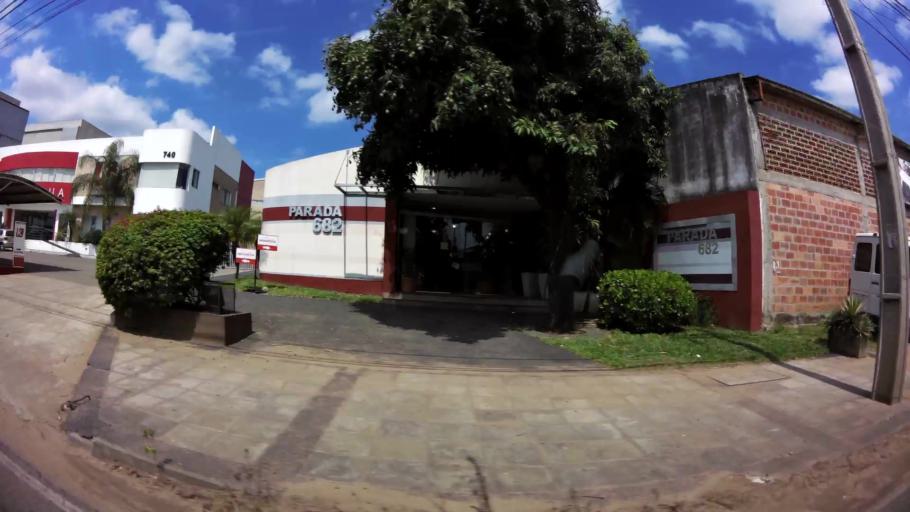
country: PY
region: Central
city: Fernando de la Mora
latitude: -25.3124
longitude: -57.5549
